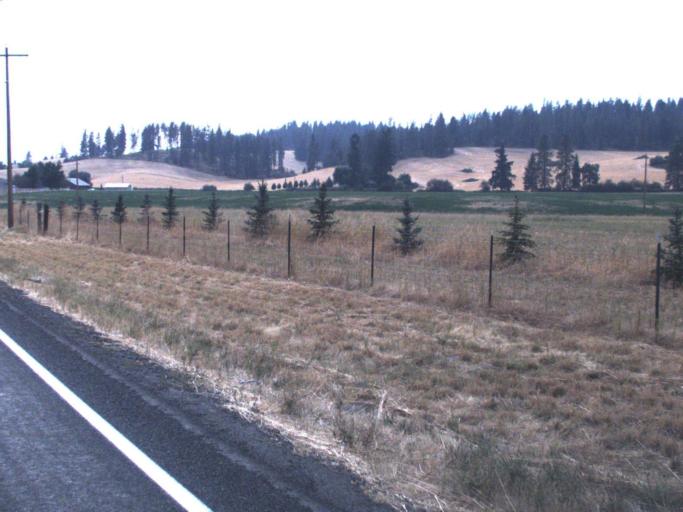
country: US
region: Washington
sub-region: Spokane County
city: Trentwood
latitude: 47.7967
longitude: -117.2434
